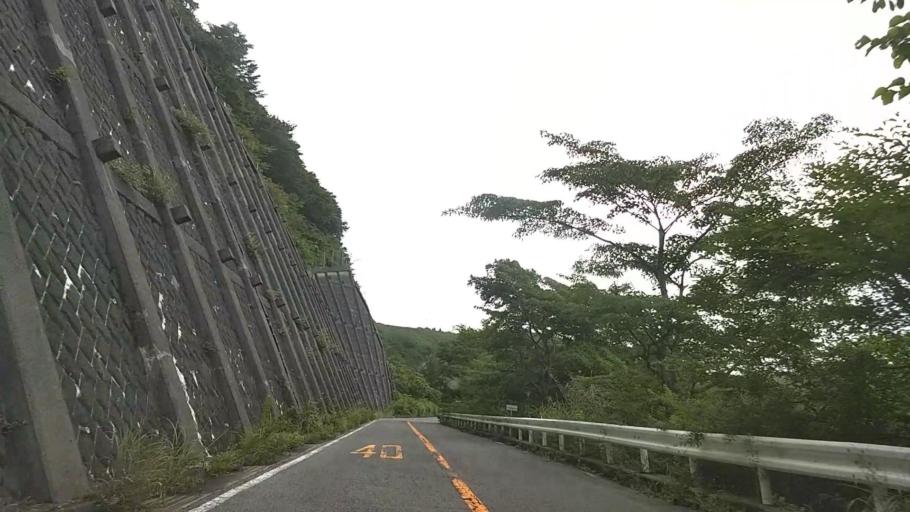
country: JP
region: Kanagawa
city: Hakone
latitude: 35.1803
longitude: 139.0576
